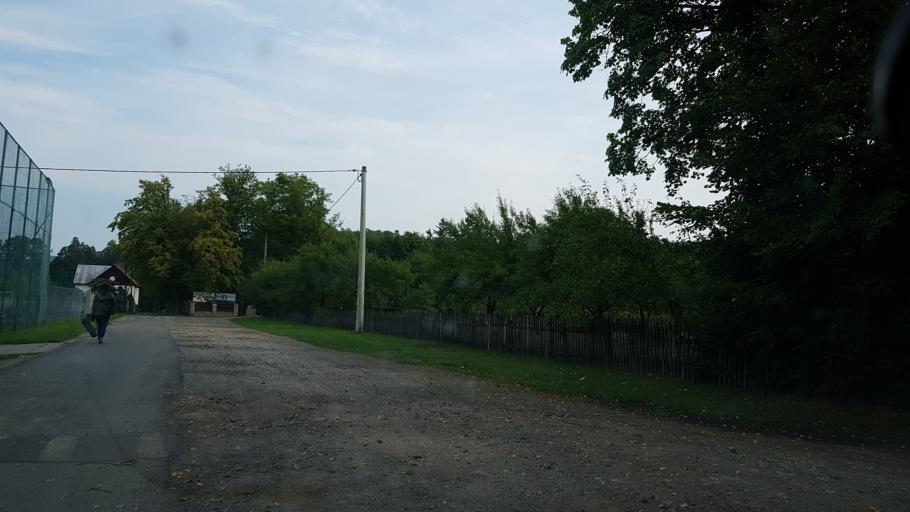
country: PL
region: Lower Silesian Voivodeship
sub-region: Powiat jeleniogorski
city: Janowice Wielkie
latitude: 50.8796
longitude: 15.9214
